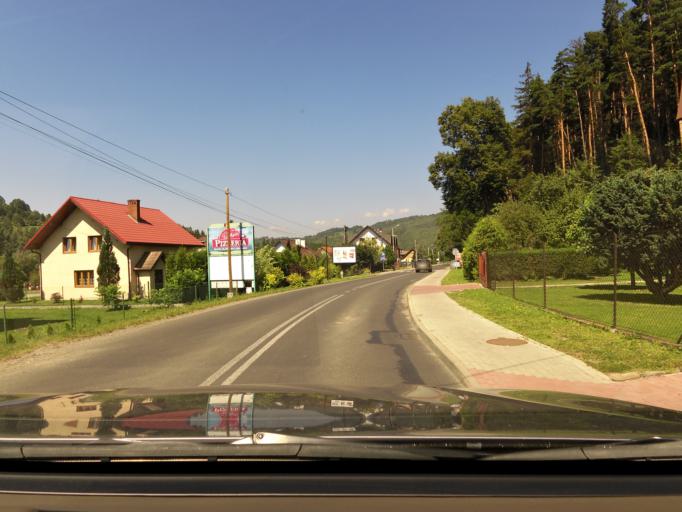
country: PL
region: Silesian Voivodeship
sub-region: Powiat zywiecki
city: Rajcza
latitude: 49.4949
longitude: 19.1059
